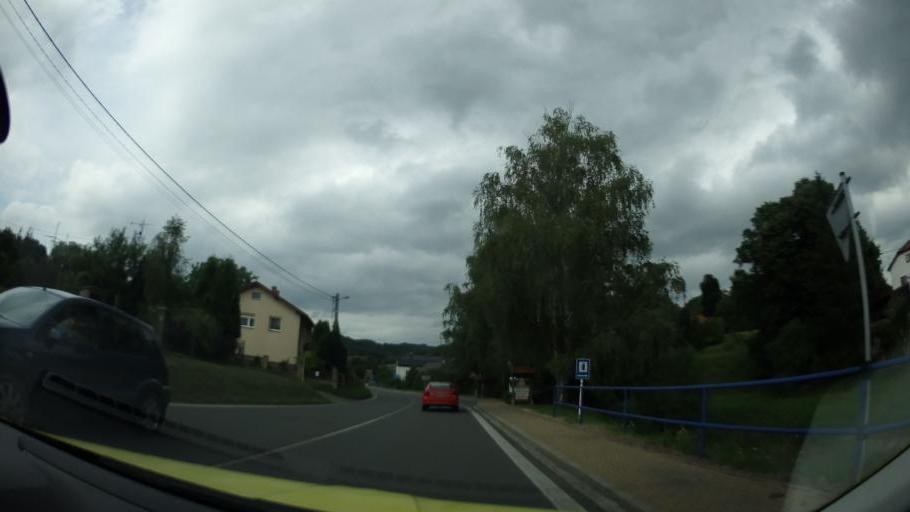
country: CZ
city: Morkov
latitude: 49.5427
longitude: 18.0600
